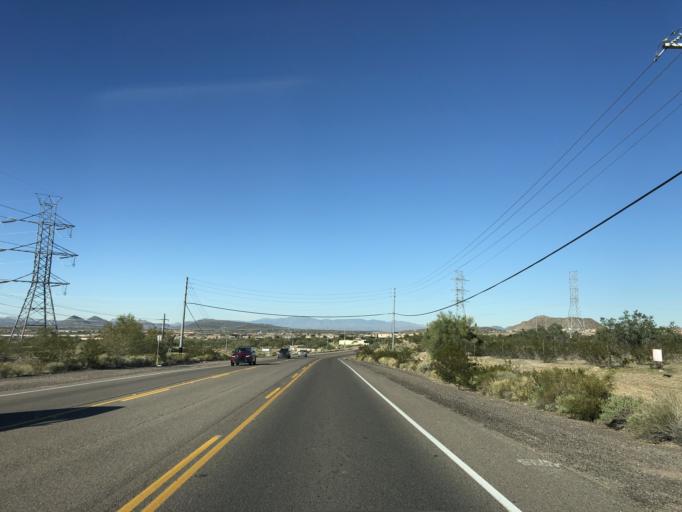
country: US
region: Arizona
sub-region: Maricopa County
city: Sun City West
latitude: 33.7035
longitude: -112.2898
